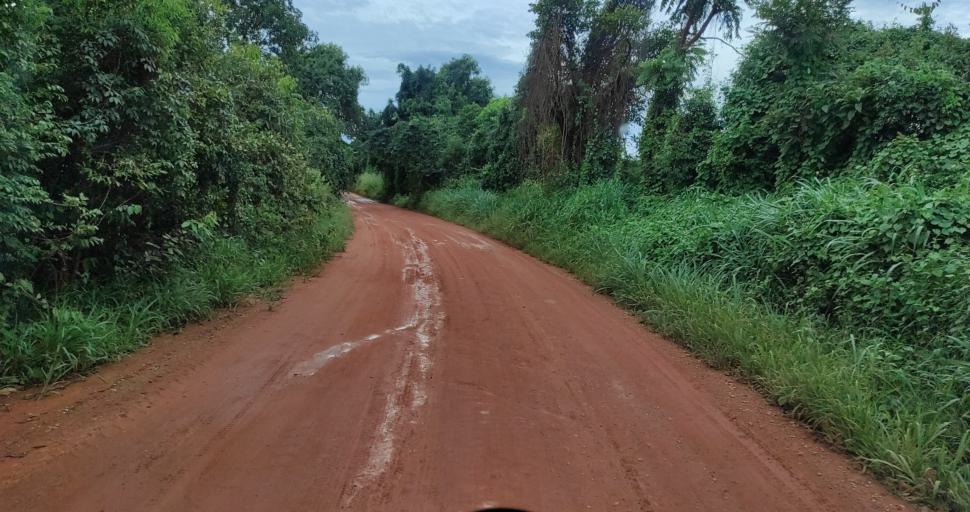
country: BR
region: Minas Gerais
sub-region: Piui
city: Piui
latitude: -20.2835
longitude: -46.3672
